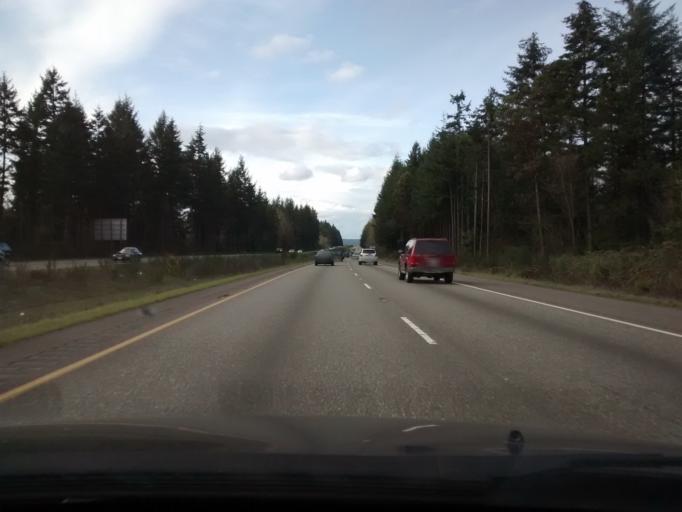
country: US
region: Washington
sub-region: Pierce County
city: Gig Harbor
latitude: 47.3389
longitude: -122.6055
